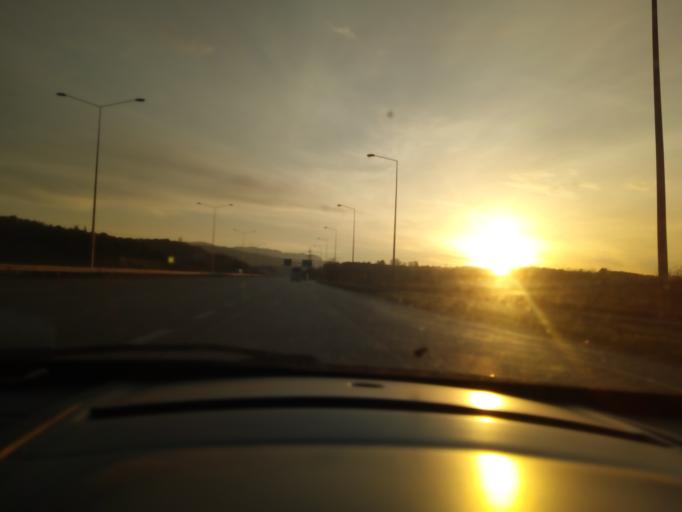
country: TR
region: Bursa
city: Demirtas
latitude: 40.2855
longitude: 29.0367
